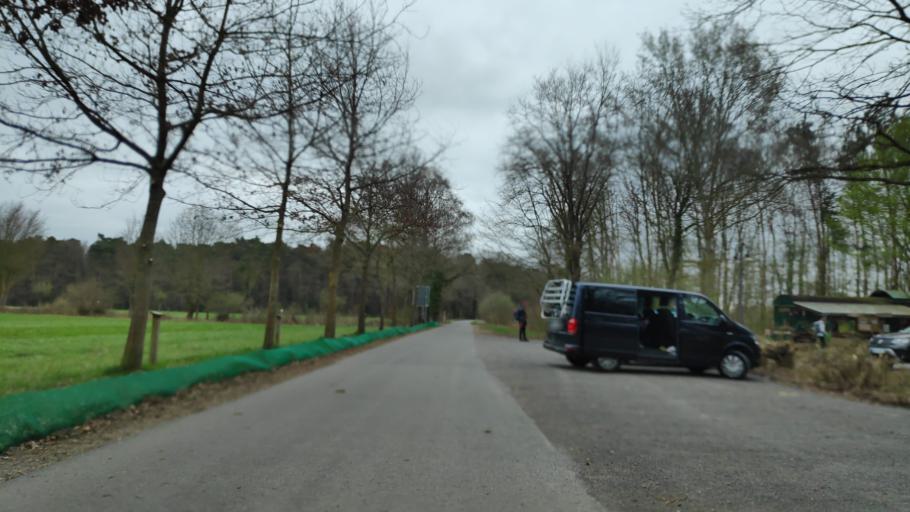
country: DE
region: North Rhine-Westphalia
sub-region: Regierungsbezirk Detmold
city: Petershagen
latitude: 52.3607
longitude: 8.9120
